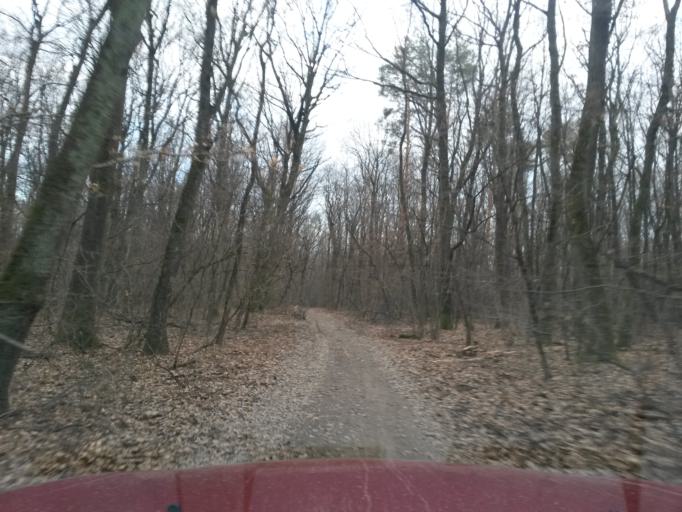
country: SK
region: Kosicky
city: Kosice
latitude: 48.6997
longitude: 21.2973
